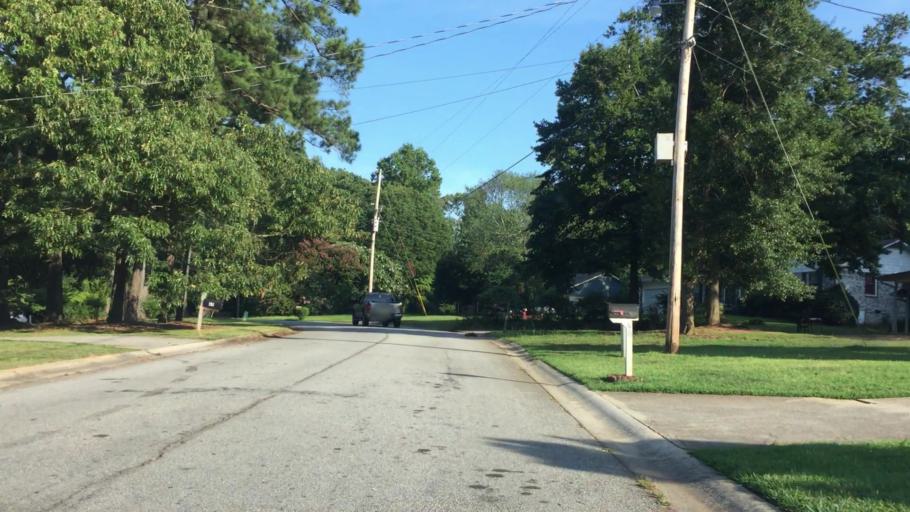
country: US
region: Georgia
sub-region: Henry County
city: Stockbridge
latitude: 33.6213
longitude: -84.2313
